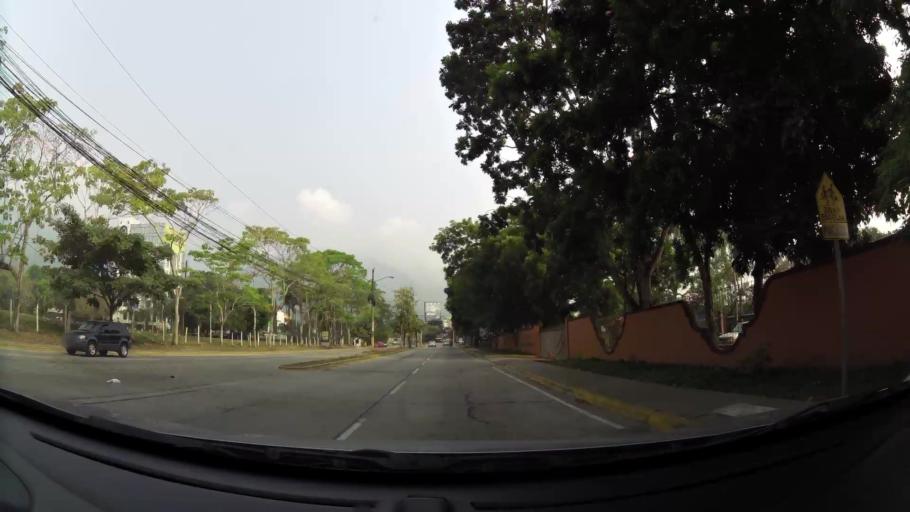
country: HN
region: Cortes
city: El Zapotal del Norte
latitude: 15.5228
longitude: -88.0362
